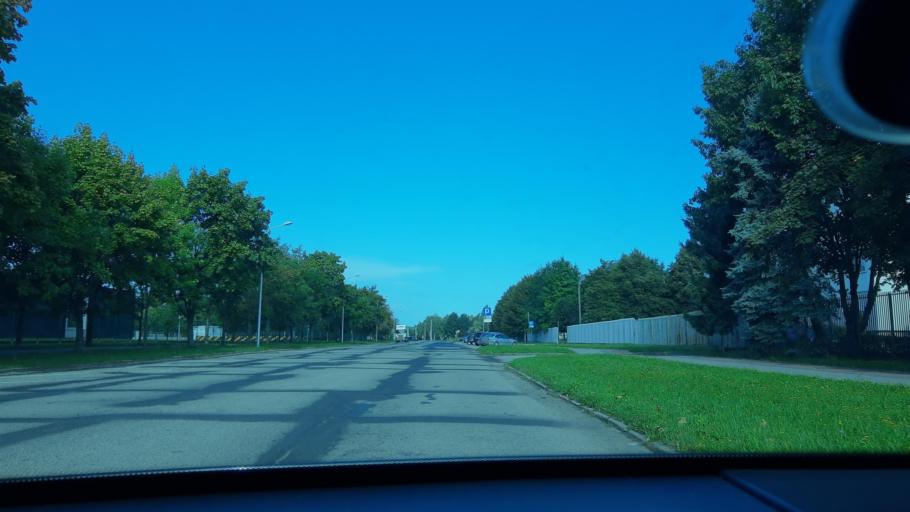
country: PL
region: Lodz Voivodeship
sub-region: Powiat sieradzki
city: Sieradz
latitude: 51.5839
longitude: 18.7148
